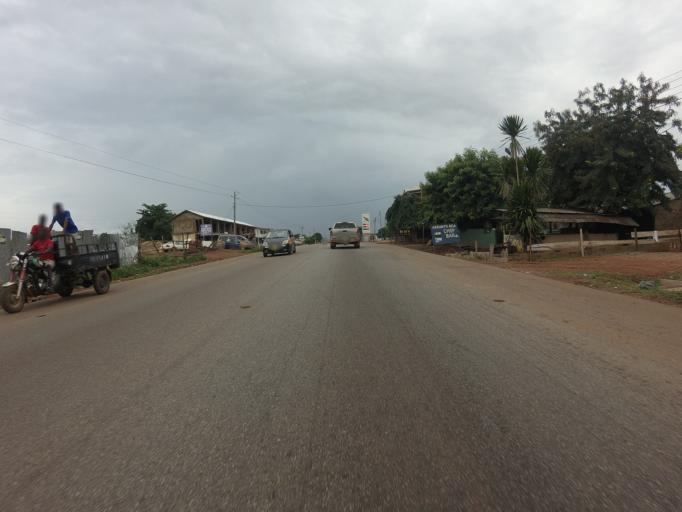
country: GH
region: Ashanti
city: Konongo
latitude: 6.6206
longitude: -1.1958
